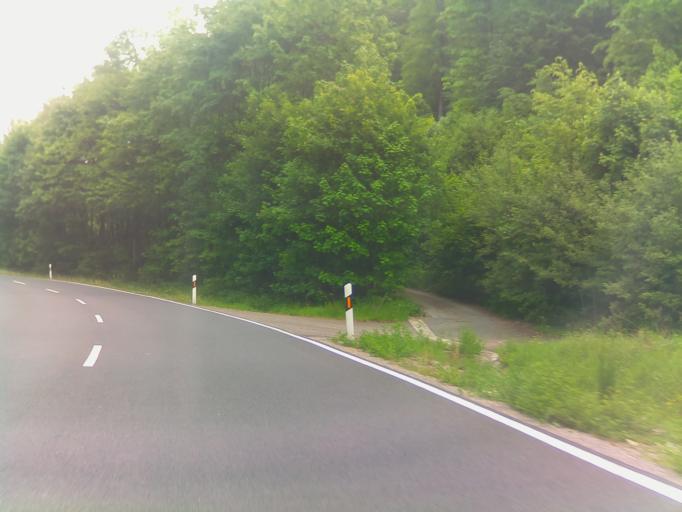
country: DE
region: Thuringia
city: Henneberg
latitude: 50.4683
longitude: 10.3236
